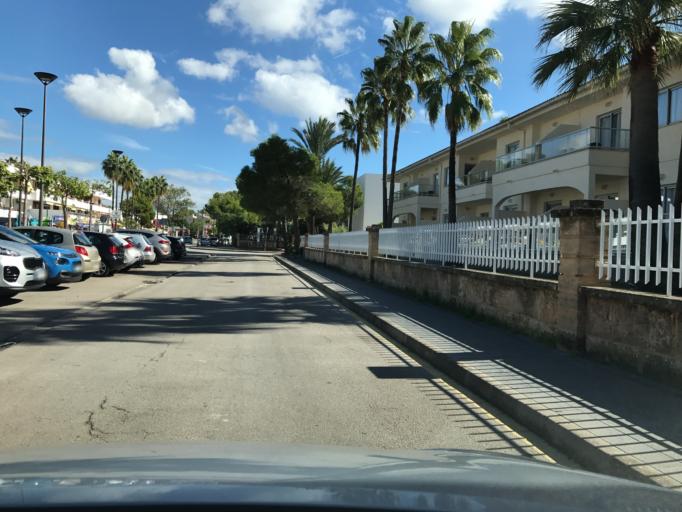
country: ES
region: Balearic Islands
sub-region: Illes Balears
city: Port d'Alcudia
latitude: 39.8337
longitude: 3.1155
